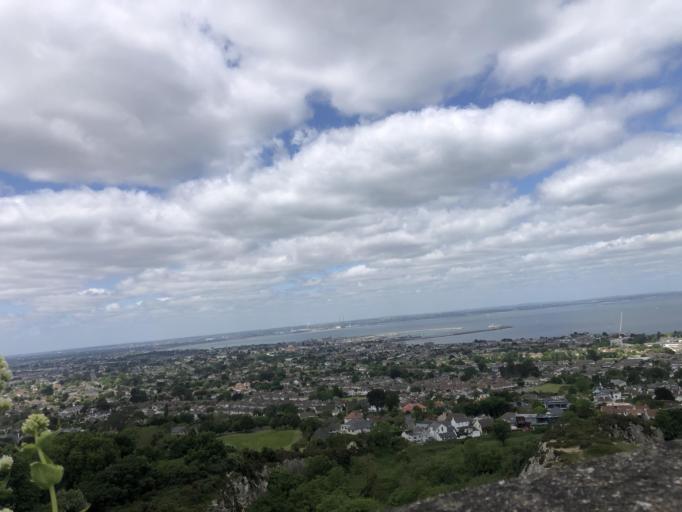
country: IE
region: Leinster
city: Dalkey
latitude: 53.2696
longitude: -6.1070
